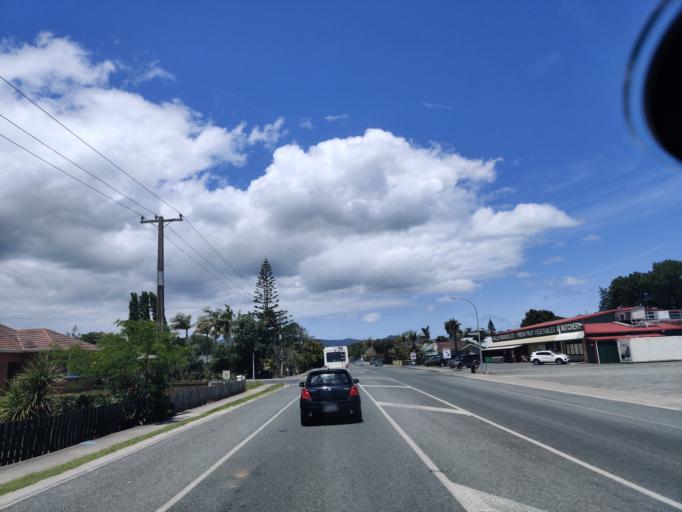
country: NZ
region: Northland
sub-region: Far North District
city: Kaitaia
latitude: -35.1005
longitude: 173.2597
